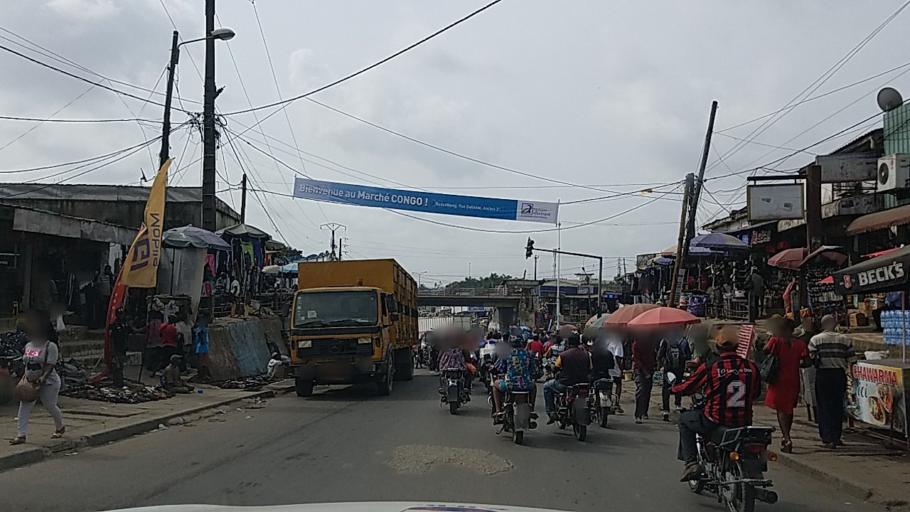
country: CM
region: Littoral
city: Douala
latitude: 4.0432
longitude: 9.7429
